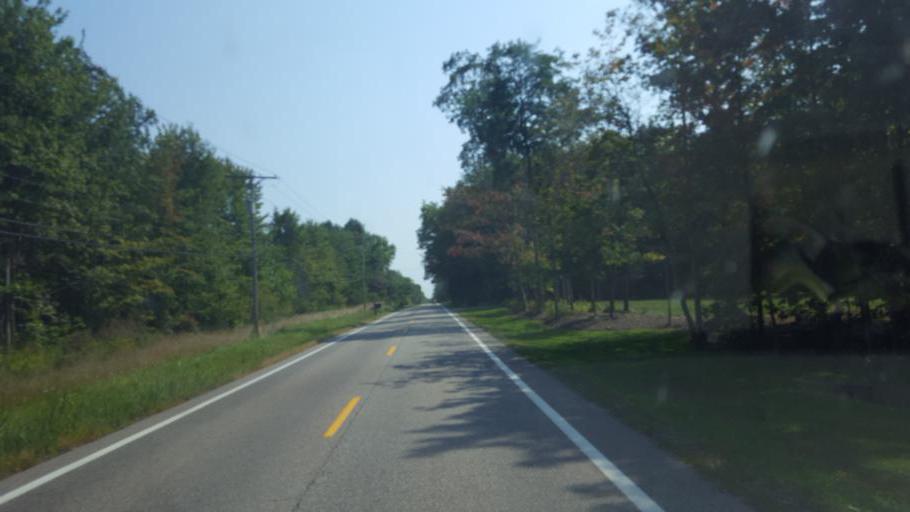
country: US
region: Ohio
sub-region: Lake County
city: Madison
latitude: 41.6662
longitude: -81.0287
